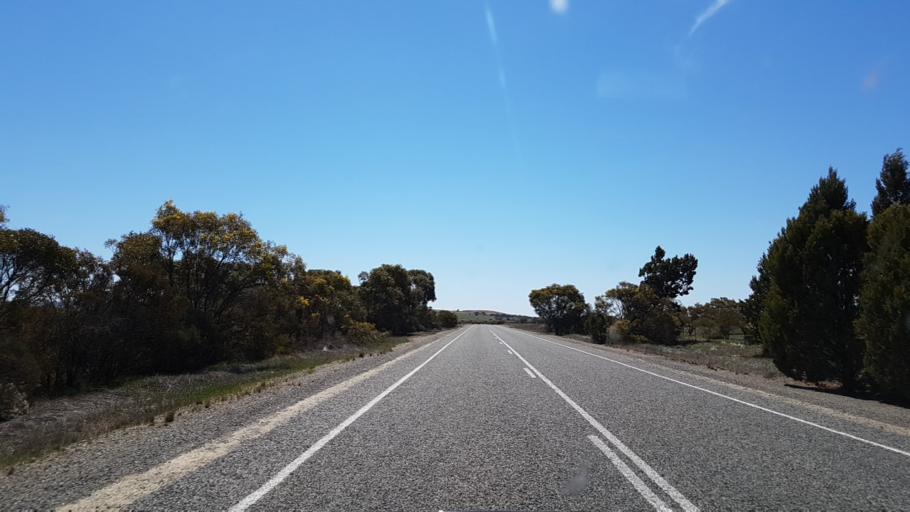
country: AU
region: South Australia
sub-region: Peterborough
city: Peterborough
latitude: -33.2423
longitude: 138.8750
